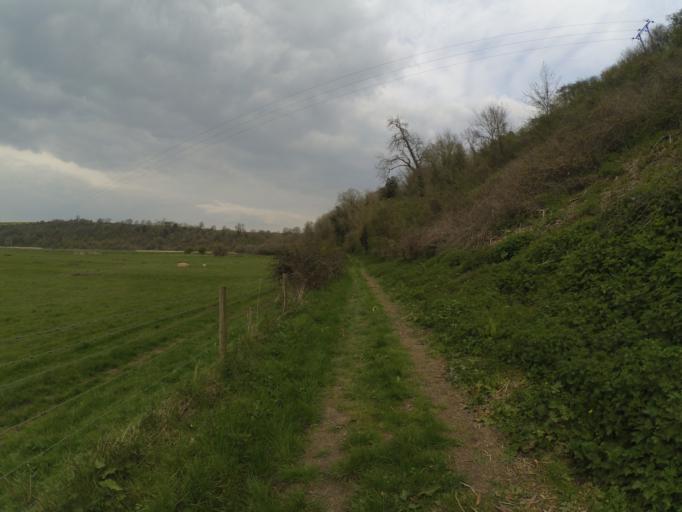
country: GB
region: England
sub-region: West Sussex
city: Arundel
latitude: 50.8802
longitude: -0.5291
